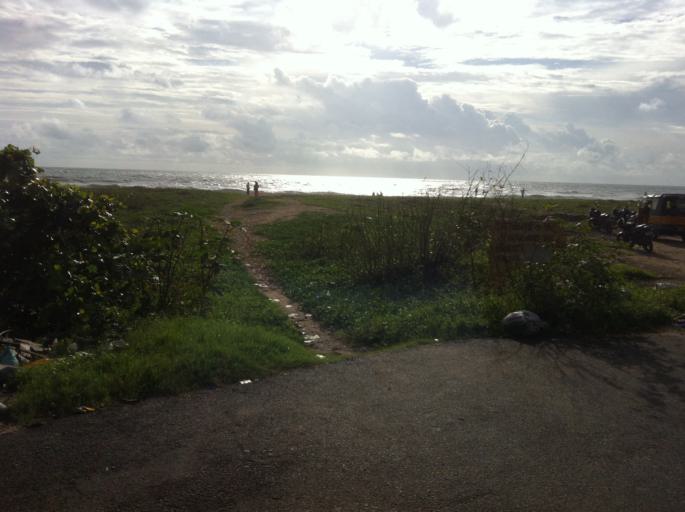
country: IN
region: Tamil Nadu
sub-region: Kancheepuram
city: Palavakkam
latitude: 12.9792
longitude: 80.2669
